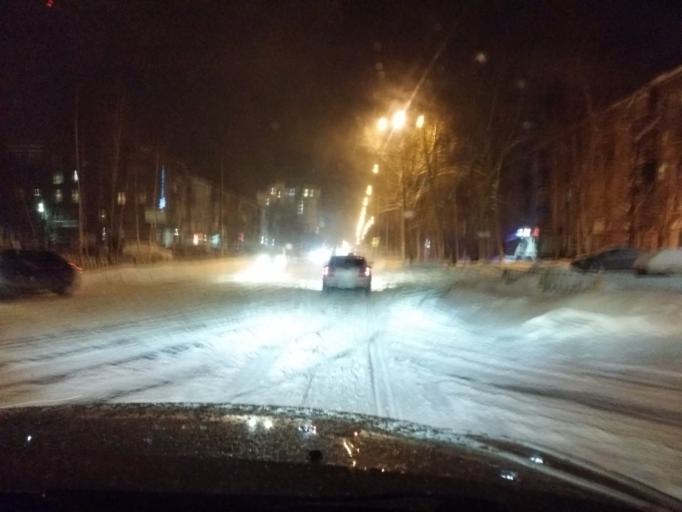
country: RU
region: Khanty-Mansiyskiy Avtonomnyy Okrug
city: Nizhnevartovsk
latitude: 60.9425
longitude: 76.5806
